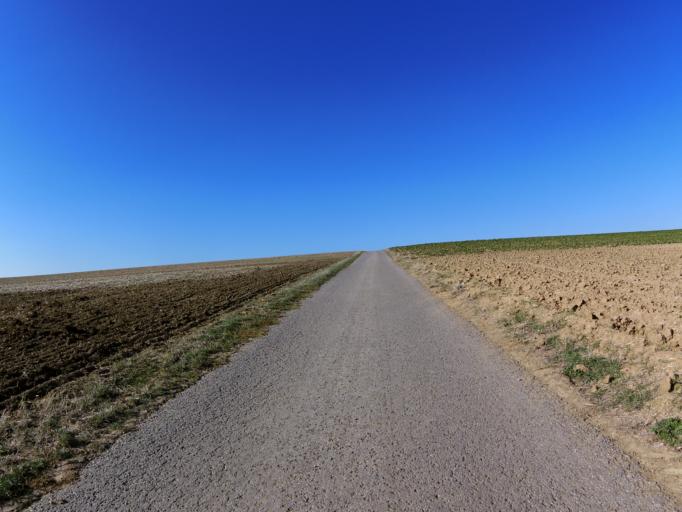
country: DE
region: Bavaria
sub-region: Regierungsbezirk Unterfranken
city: Eibelstadt
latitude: 49.7026
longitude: 9.9795
